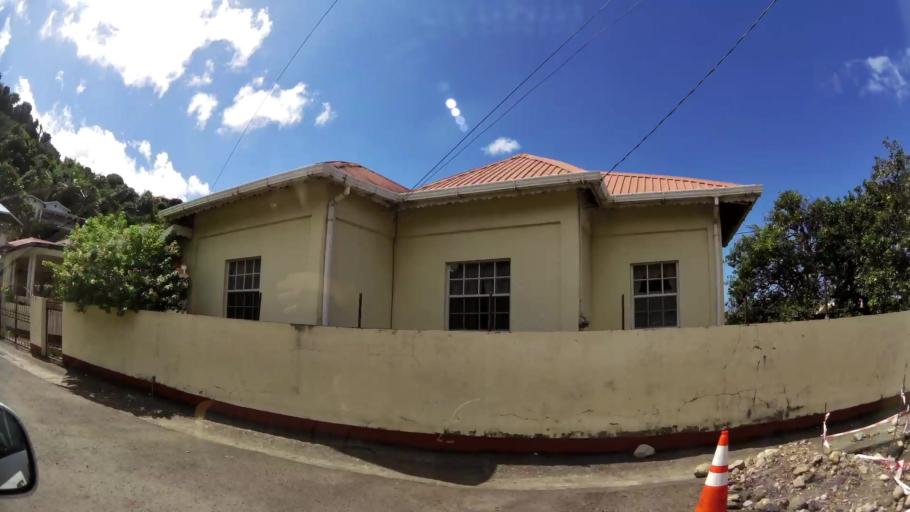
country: GD
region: Saint John
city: Gouyave
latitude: 12.1638
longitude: -61.7298
